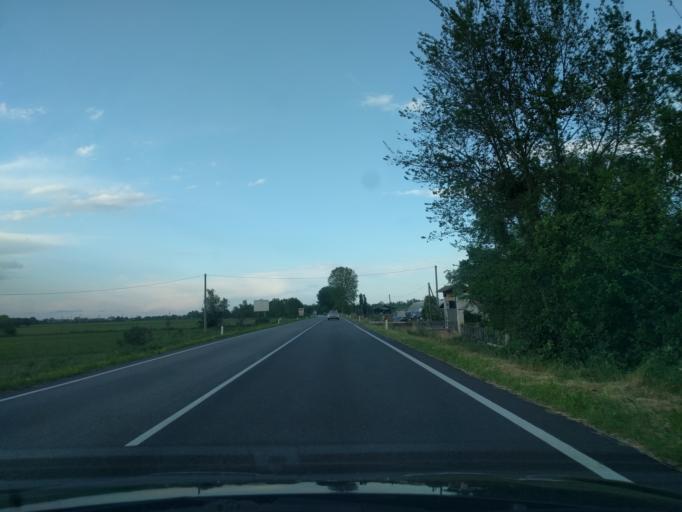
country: IT
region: Emilia-Romagna
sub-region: Provincia di Ferrara
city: Ro
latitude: 44.9373
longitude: 11.7301
